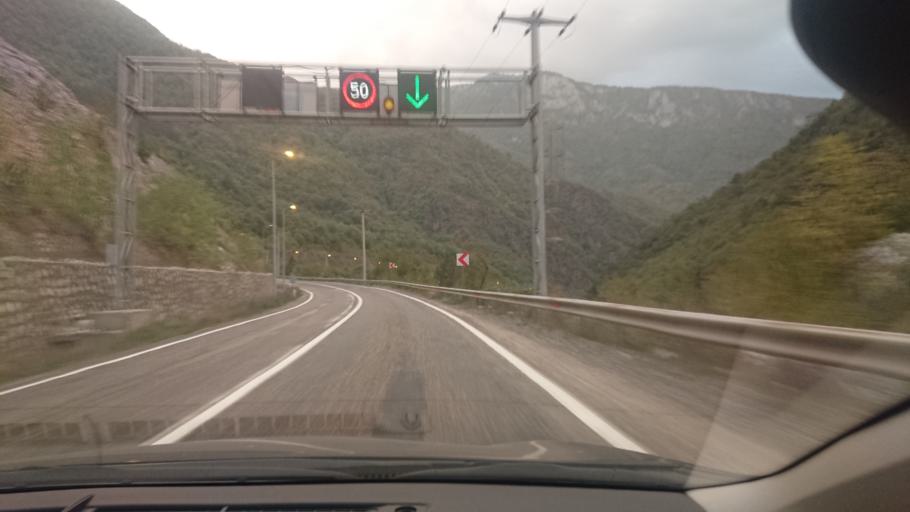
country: TR
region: Karabuk
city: Yenice
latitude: 41.1586
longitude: 32.4720
